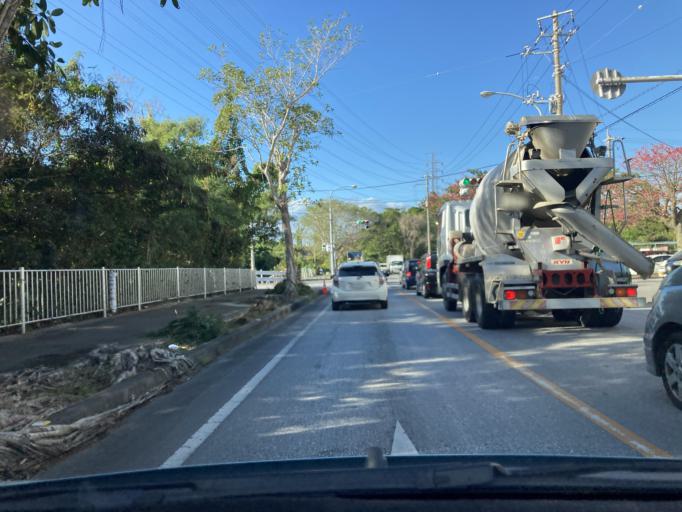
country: JP
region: Okinawa
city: Gushikawa
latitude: 26.3629
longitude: 127.8430
